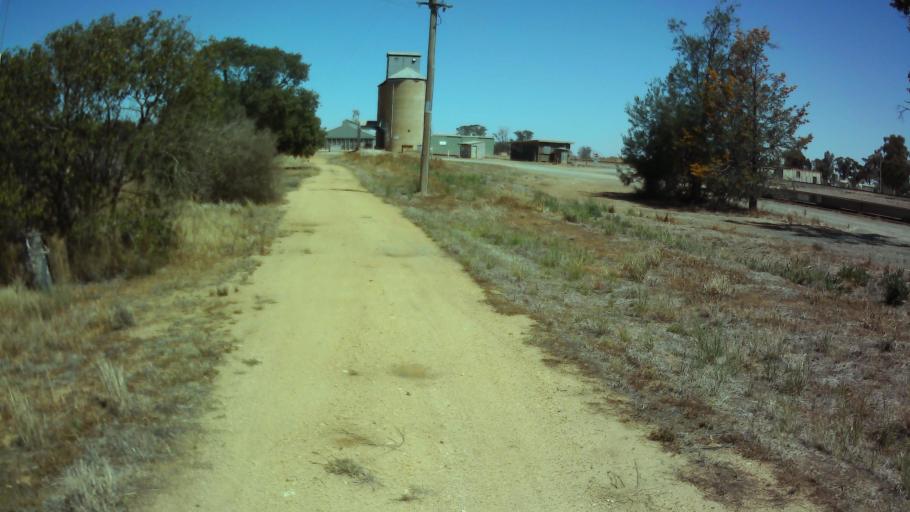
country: AU
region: New South Wales
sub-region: Weddin
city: Grenfell
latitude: -34.0104
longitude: 147.7957
